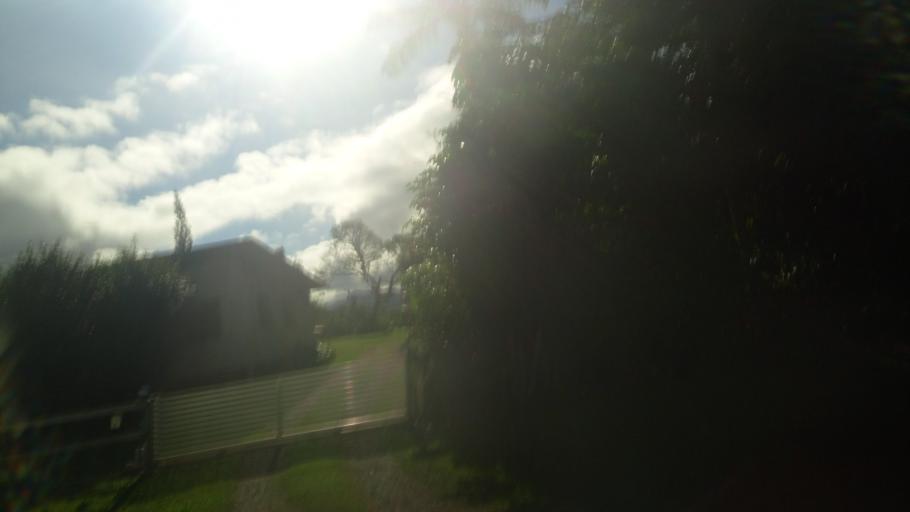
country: AU
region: Queensland
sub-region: Cassowary Coast
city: Innisfail
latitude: -17.5368
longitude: 145.9669
